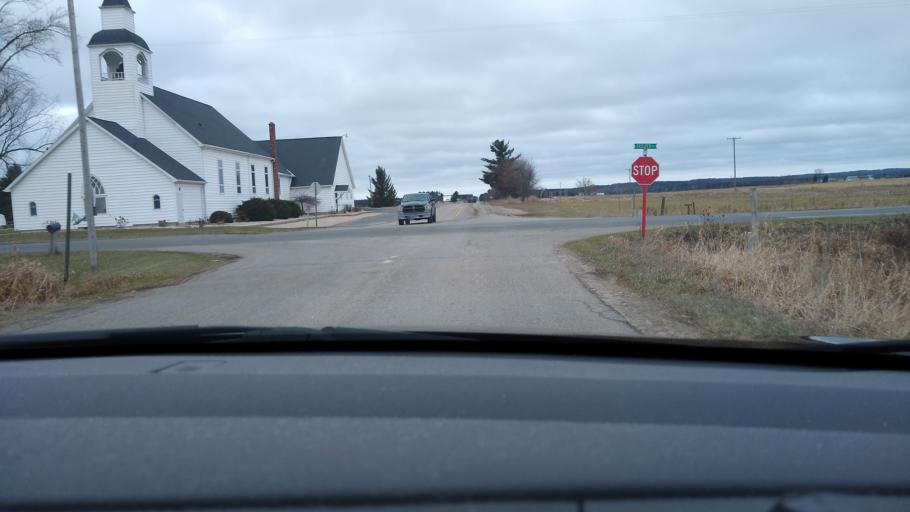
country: US
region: Michigan
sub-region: Missaukee County
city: Lake City
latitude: 44.2429
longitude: -85.0535
